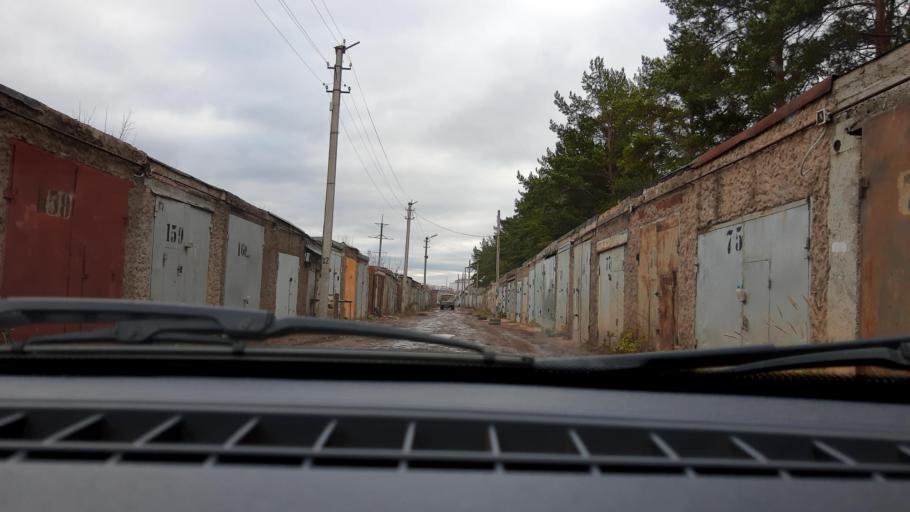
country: RU
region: Bashkortostan
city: Mikhaylovka
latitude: 54.7882
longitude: 55.8691
